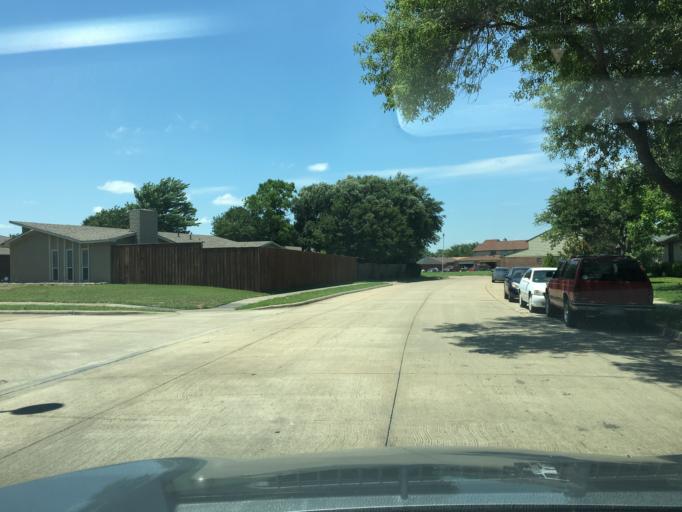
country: US
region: Texas
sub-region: Dallas County
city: Richardson
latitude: 32.9494
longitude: -96.6783
